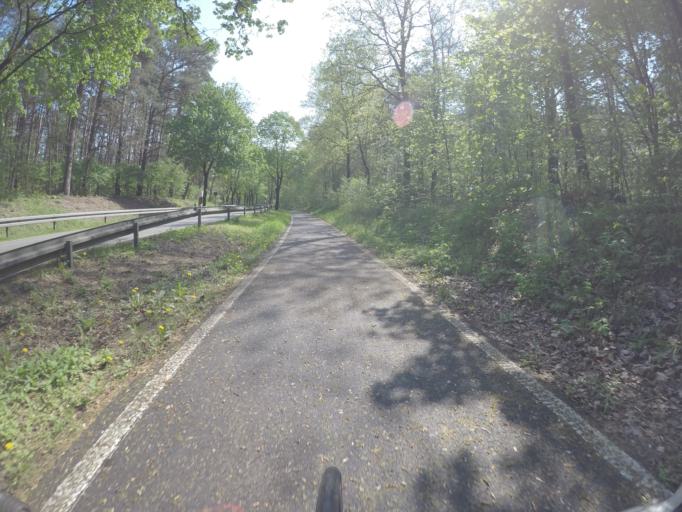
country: DE
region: Brandenburg
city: Marienwerder
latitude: 52.7921
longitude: 13.5355
